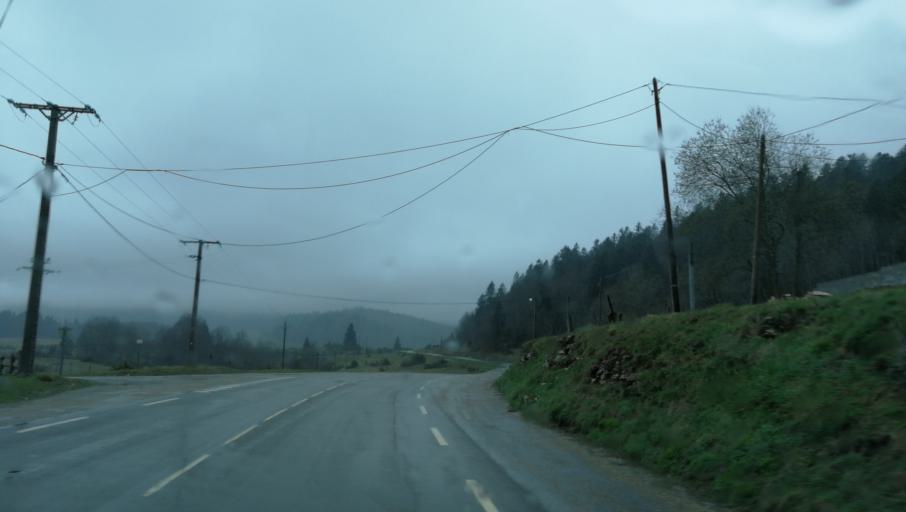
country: FR
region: Rhone-Alpes
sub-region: Departement de la Drome
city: Saint-Jean-en-Royans
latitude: 44.9496
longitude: 5.3224
